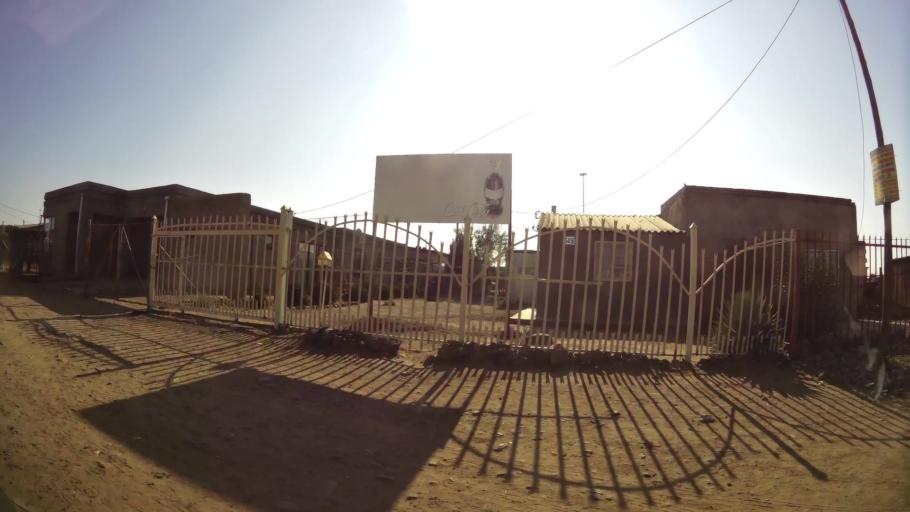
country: ZA
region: Orange Free State
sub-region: Mangaung Metropolitan Municipality
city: Bloemfontein
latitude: -29.1959
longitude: 26.2296
